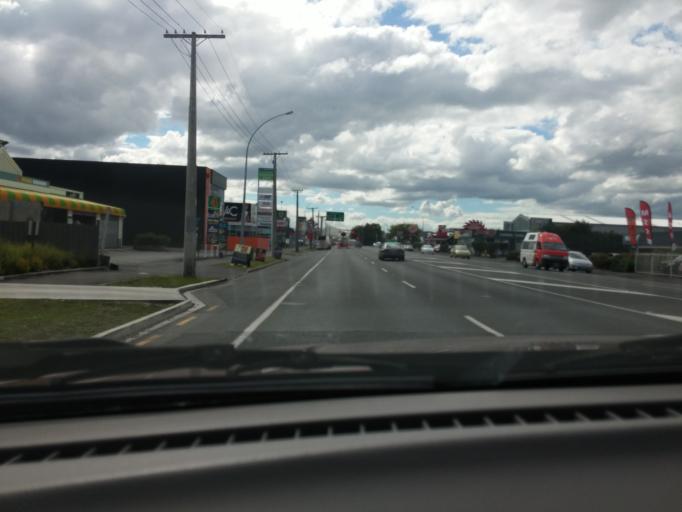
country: NZ
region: Waikato
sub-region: Hamilton City
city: Hamilton
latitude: -37.7917
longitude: 175.2601
